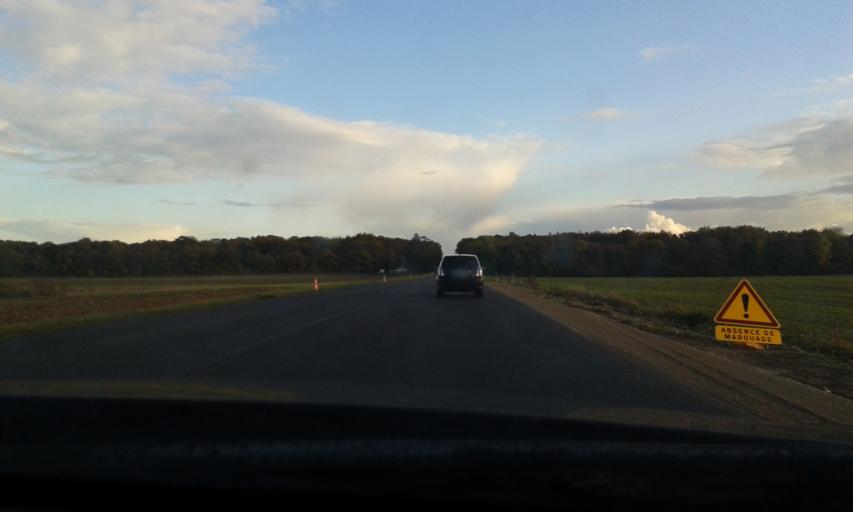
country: FR
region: Centre
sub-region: Departement d'Eure-et-Loir
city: Sours
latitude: 48.3988
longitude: 1.5572
